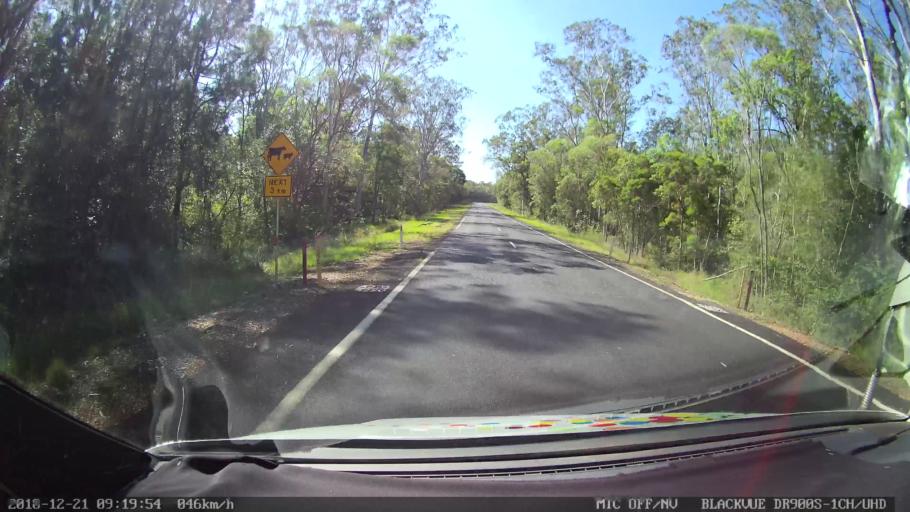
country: AU
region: New South Wales
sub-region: Clarence Valley
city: Maclean
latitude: -29.3098
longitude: 152.9977
